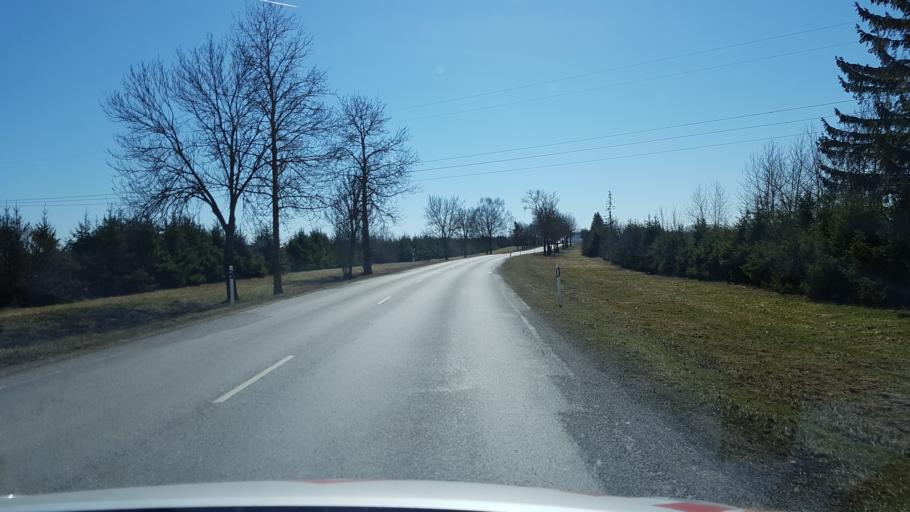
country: EE
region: Laeaene-Virumaa
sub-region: Rakvere linn
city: Rakvere
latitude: 59.3791
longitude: 26.3915
